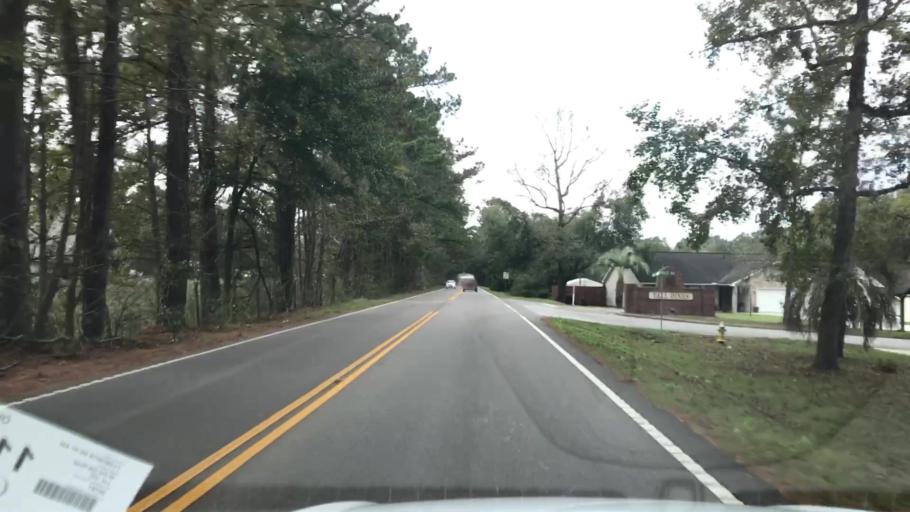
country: US
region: South Carolina
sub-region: Berkeley County
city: Ladson
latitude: 33.0055
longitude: -80.1022
